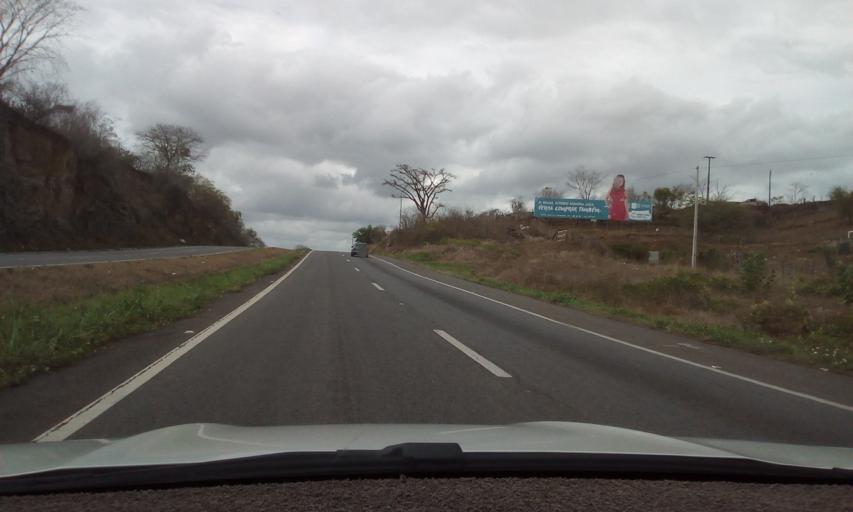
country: BR
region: Paraiba
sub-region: Massaranduba
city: Massaranduba
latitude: -7.2693
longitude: -35.7219
